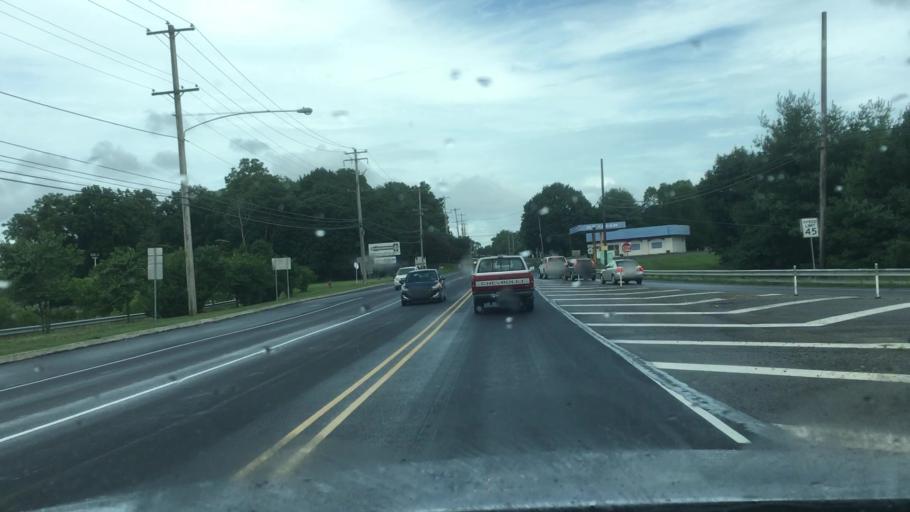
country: US
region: Pennsylvania
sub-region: Chester County
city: Avondale
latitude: 39.8342
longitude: -75.7934
